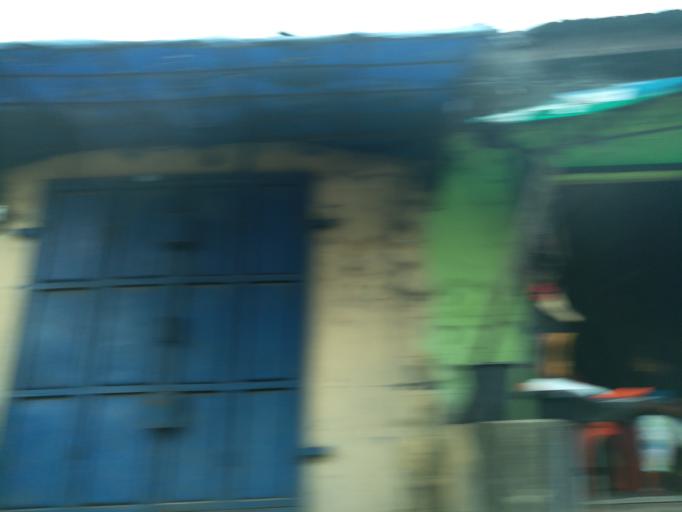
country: NG
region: Rivers
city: Port Harcourt
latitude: 4.8159
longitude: 7.0231
